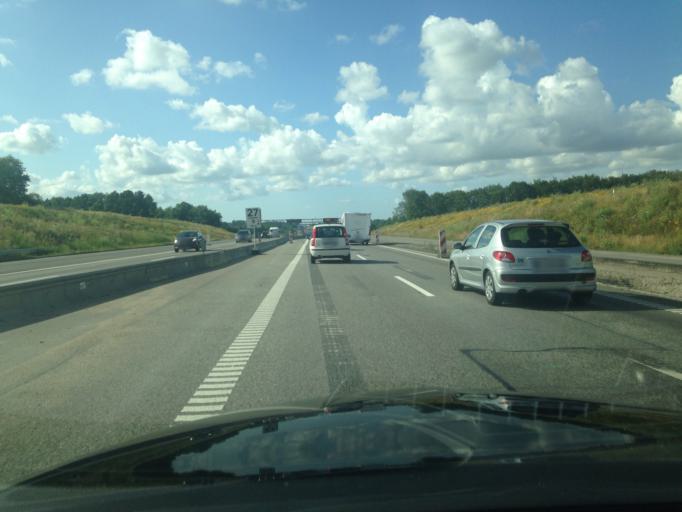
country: DK
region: Capital Region
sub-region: Rudersdal Kommune
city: Trorod
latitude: 55.8332
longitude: 12.5222
